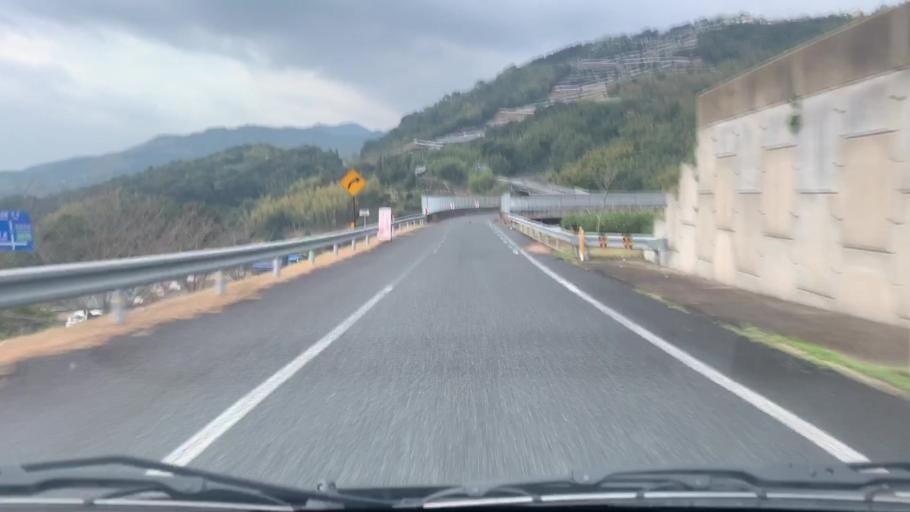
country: JP
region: Nagasaki
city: Nagasaki-shi
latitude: 32.7284
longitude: 129.9052
